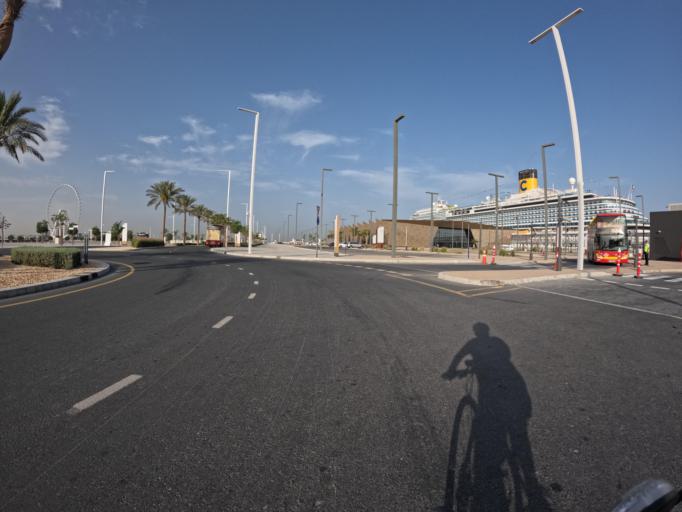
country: AE
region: Dubai
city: Dubai
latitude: 25.0928
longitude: 55.1311
